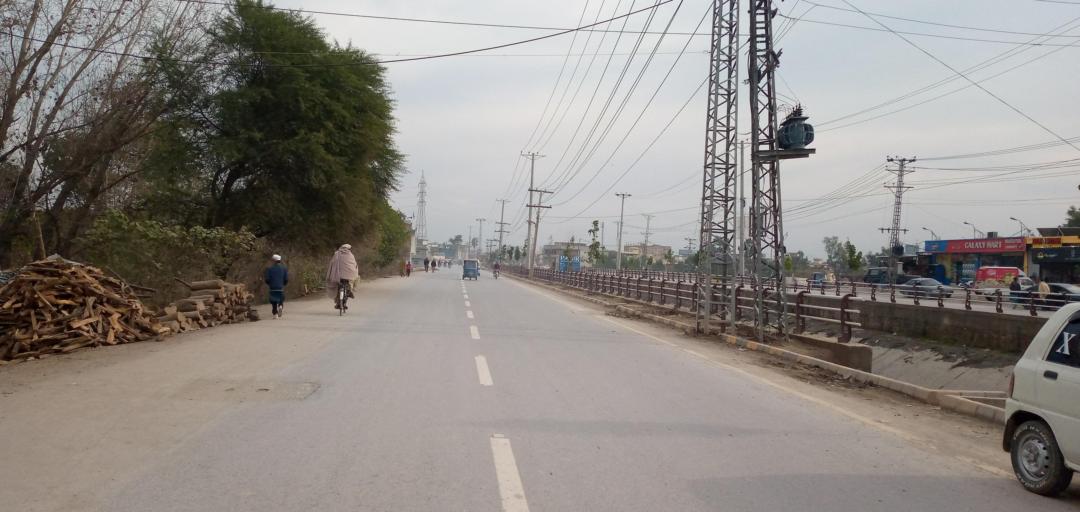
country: PK
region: Khyber Pakhtunkhwa
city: Peshawar
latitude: 34.0054
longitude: 71.4640
